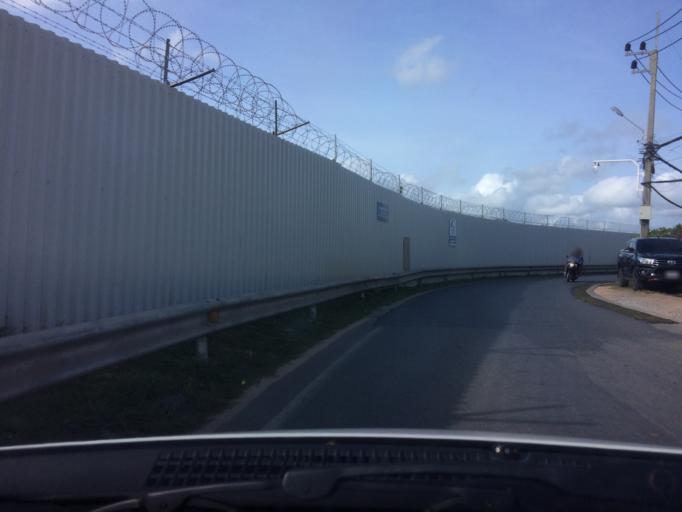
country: TH
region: Phuket
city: Thalang
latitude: 8.1105
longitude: 98.3098
